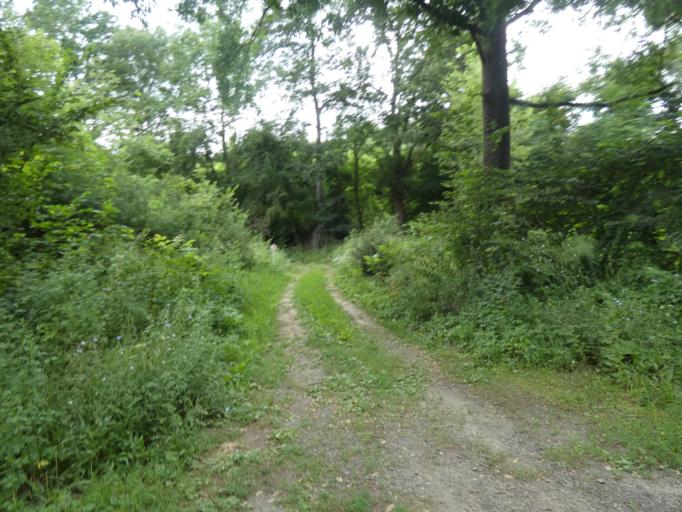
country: HU
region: Pest
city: Szob
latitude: 47.8215
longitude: 18.8974
